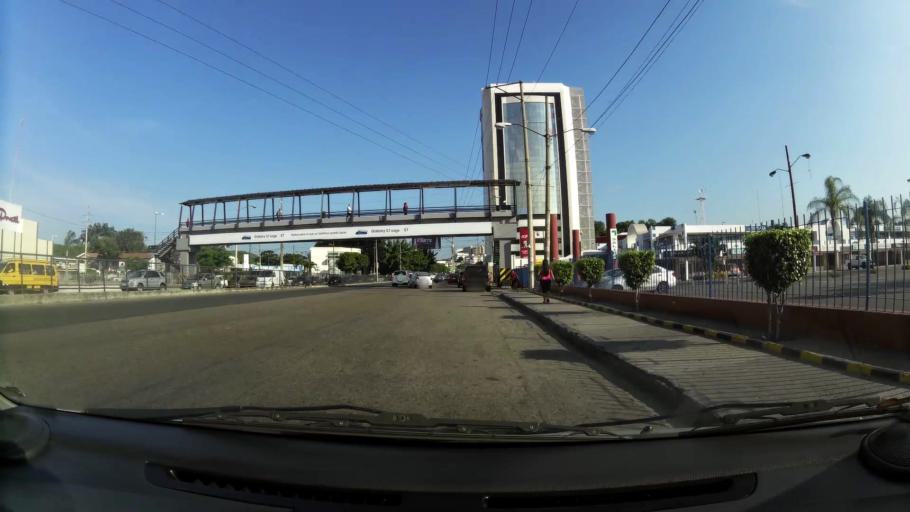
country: EC
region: Guayas
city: Guayaquil
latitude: -2.1694
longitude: -79.8998
